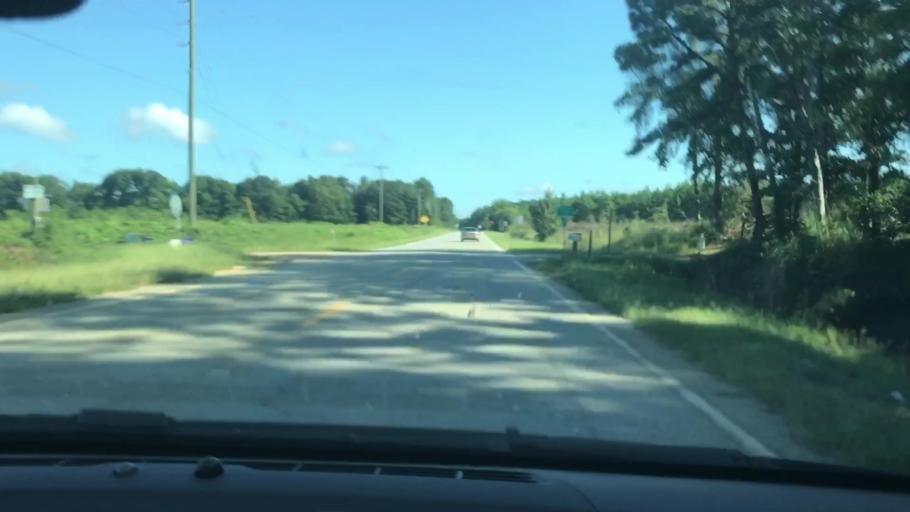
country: US
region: Georgia
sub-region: Quitman County
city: Georgetown
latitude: 31.7790
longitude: -85.0917
